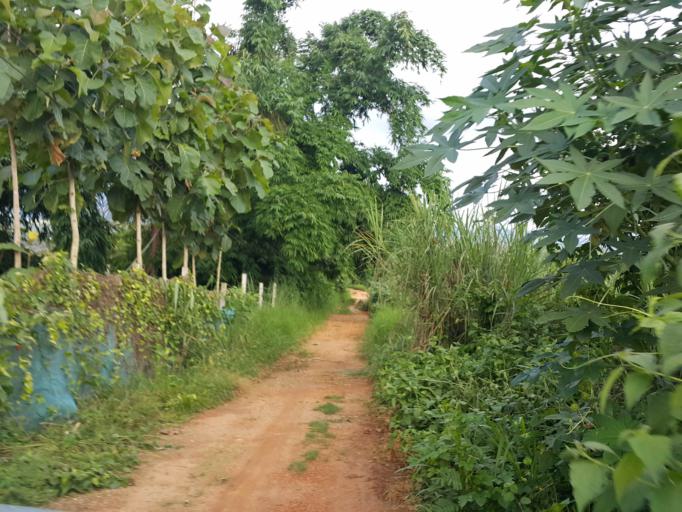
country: TH
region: Chiang Mai
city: Mae Chaem
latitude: 18.4931
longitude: 98.3642
